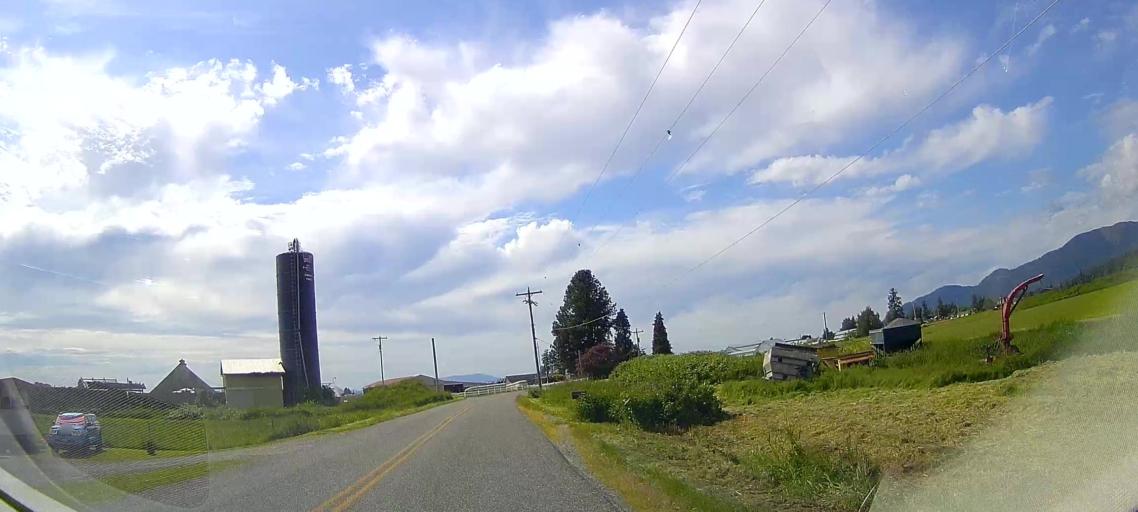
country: US
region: Washington
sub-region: Skagit County
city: Burlington
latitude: 48.5363
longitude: -122.3869
